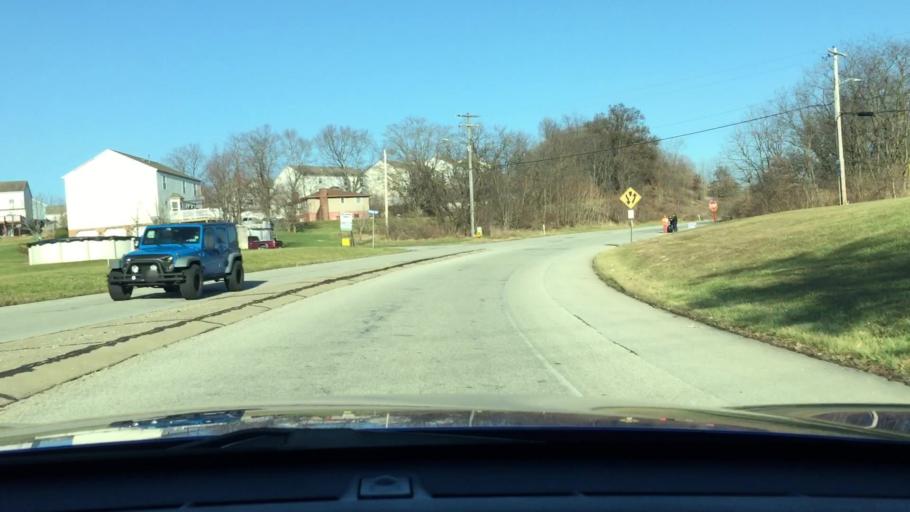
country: US
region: Pennsylvania
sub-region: Westmoreland County
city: New Stanton
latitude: 40.2298
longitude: -79.6081
